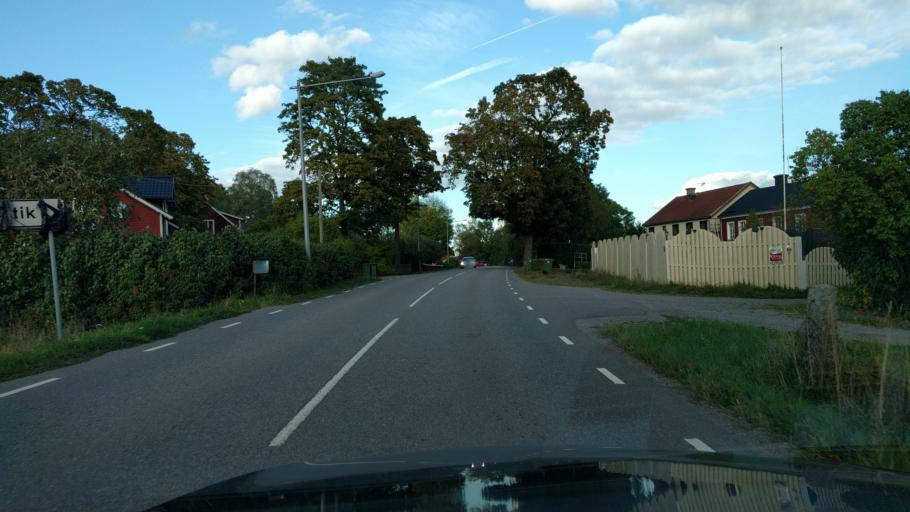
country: SE
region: Uppsala
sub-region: Osthammars Kommun
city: Bjorklinge
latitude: 60.1551
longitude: 17.5914
